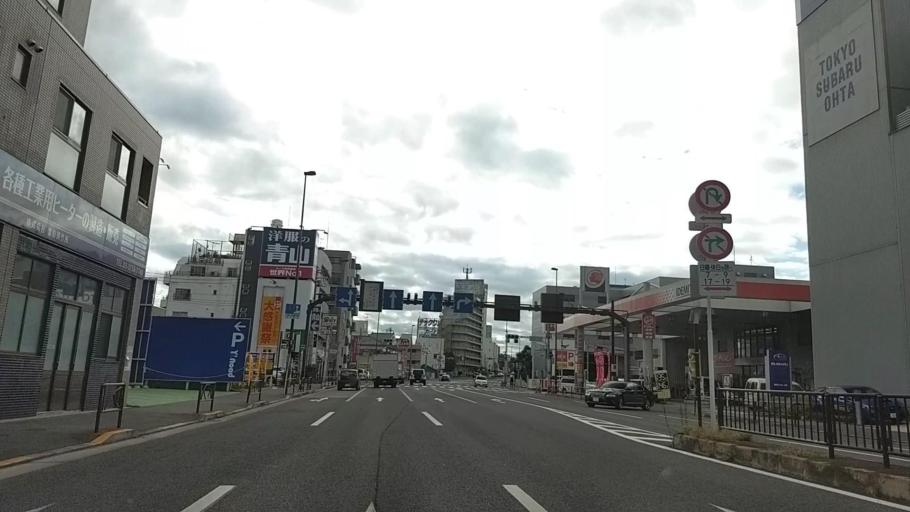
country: JP
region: Kanagawa
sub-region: Kawasaki-shi
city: Kawasaki
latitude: 35.5608
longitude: 139.6972
